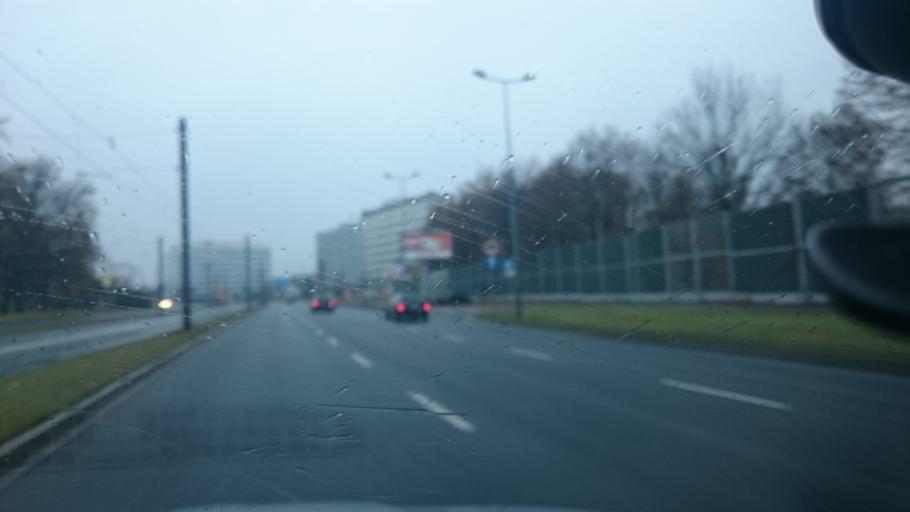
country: PL
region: Lesser Poland Voivodeship
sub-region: Krakow
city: Krakow
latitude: 50.0600
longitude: 19.9598
